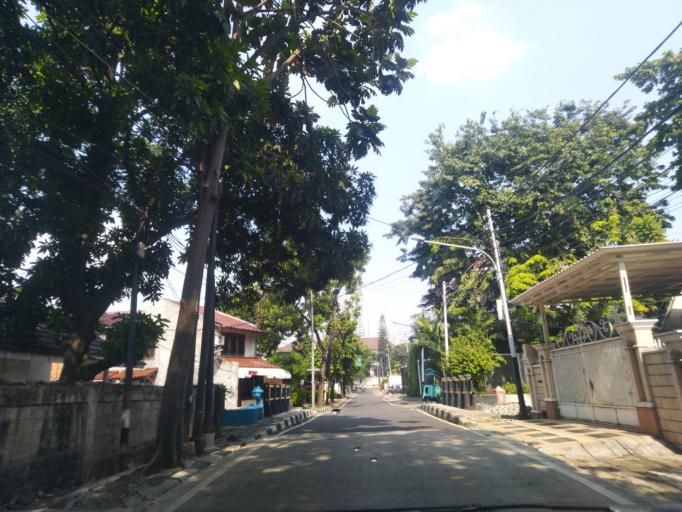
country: ID
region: Jakarta Raya
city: Jakarta
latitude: -6.2367
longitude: 106.7938
